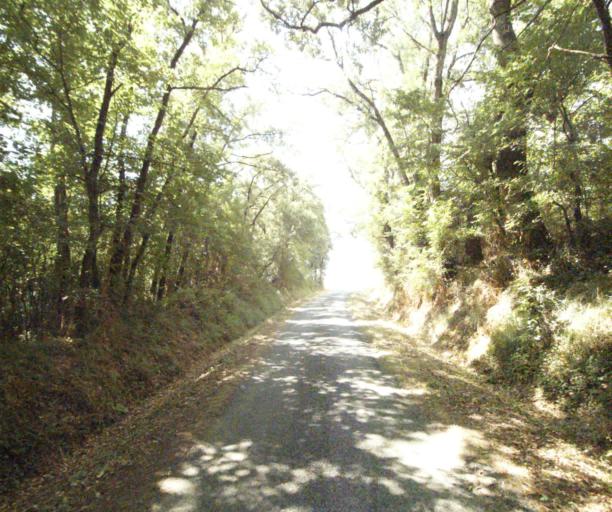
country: FR
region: Midi-Pyrenees
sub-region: Departement de la Haute-Garonne
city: Auriac-sur-Vendinelle
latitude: 43.4754
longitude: 1.7965
